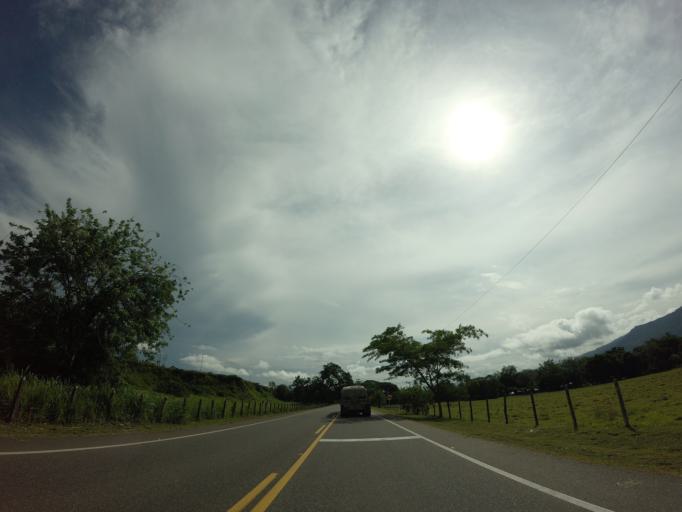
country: CO
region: Tolima
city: Honda
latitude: 5.3085
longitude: -74.7385
